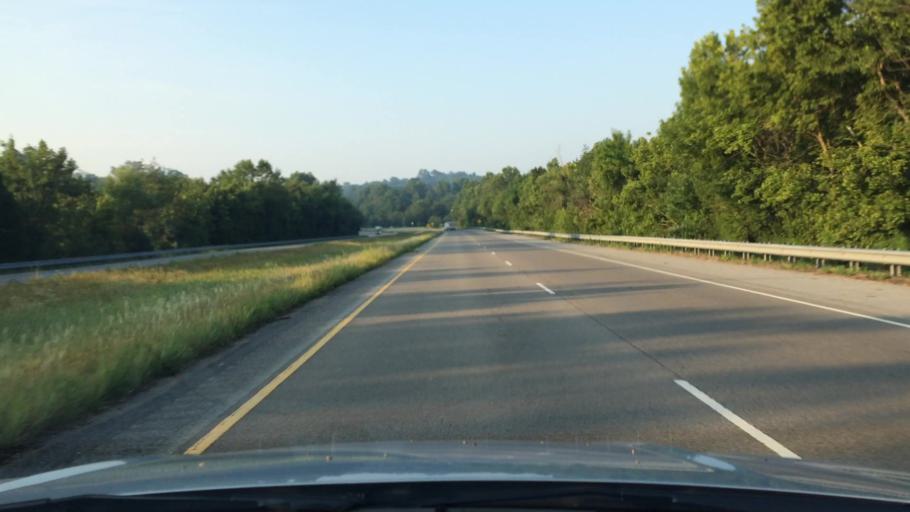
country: US
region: Tennessee
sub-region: Giles County
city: Pulaski
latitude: 35.1925
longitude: -87.0645
